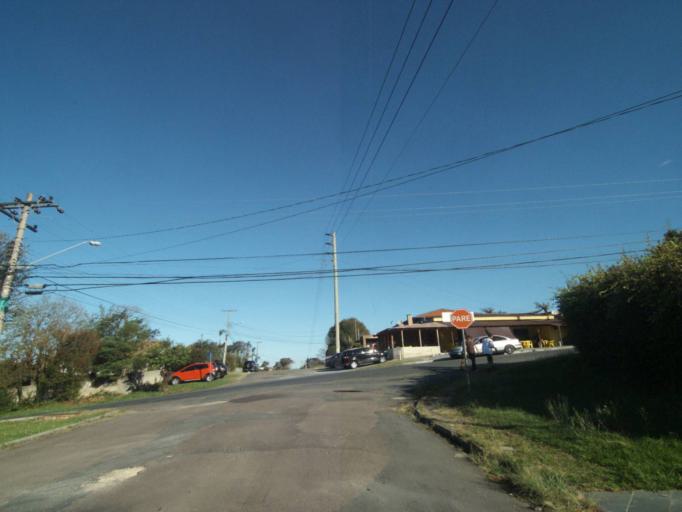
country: BR
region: Parana
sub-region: Curitiba
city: Curitiba
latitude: -25.3804
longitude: -49.2564
